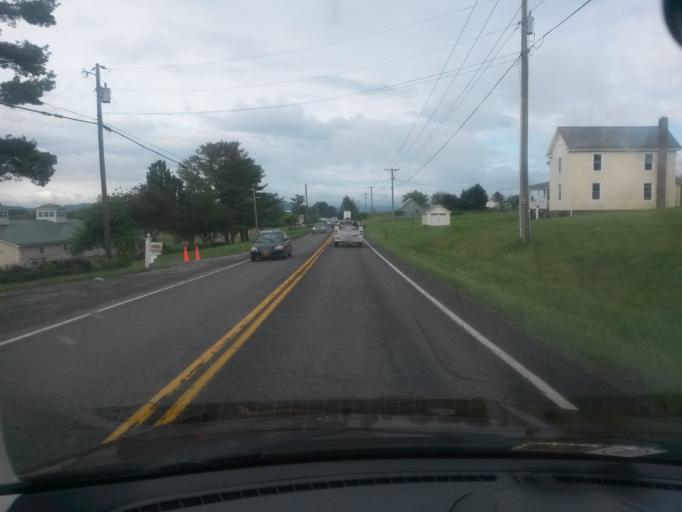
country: US
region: Virginia
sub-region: Montgomery County
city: Christiansburg
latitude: 37.0934
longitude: -80.4482
